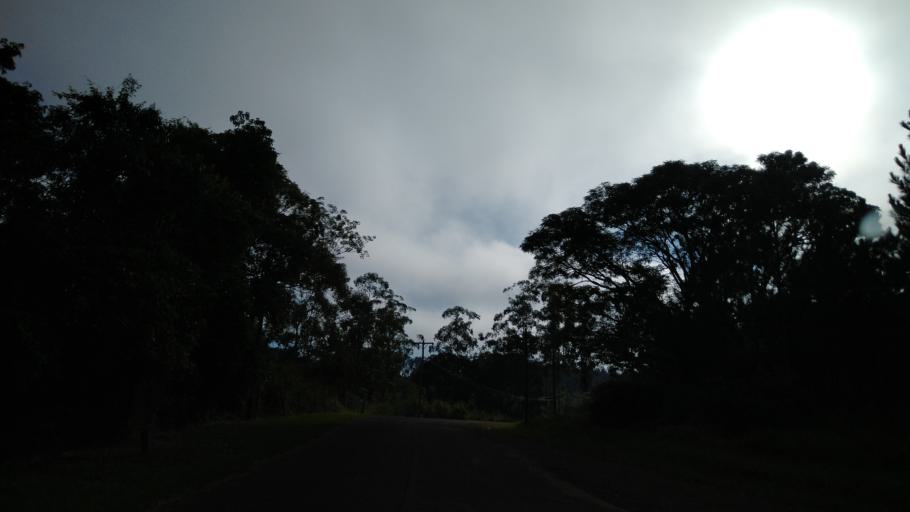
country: AR
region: Misiones
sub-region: Departamento de Montecarlo
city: Montecarlo
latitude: -26.5682
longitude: -54.7974
